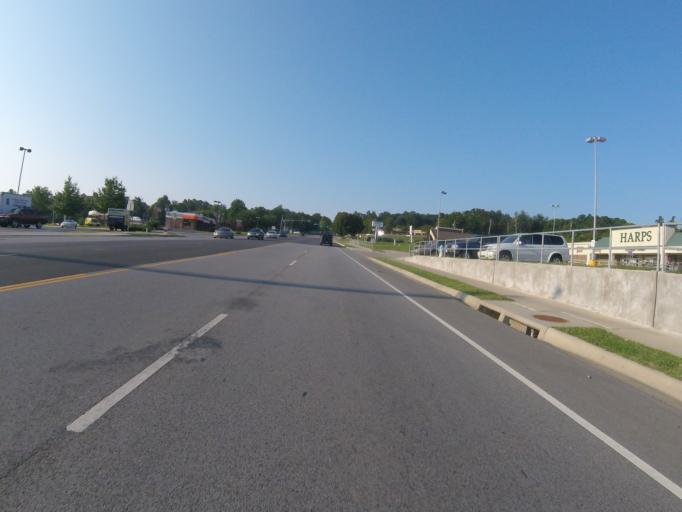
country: US
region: Arkansas
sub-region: Washington County
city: Fayetteville
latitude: 36.0790
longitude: -94.1754
